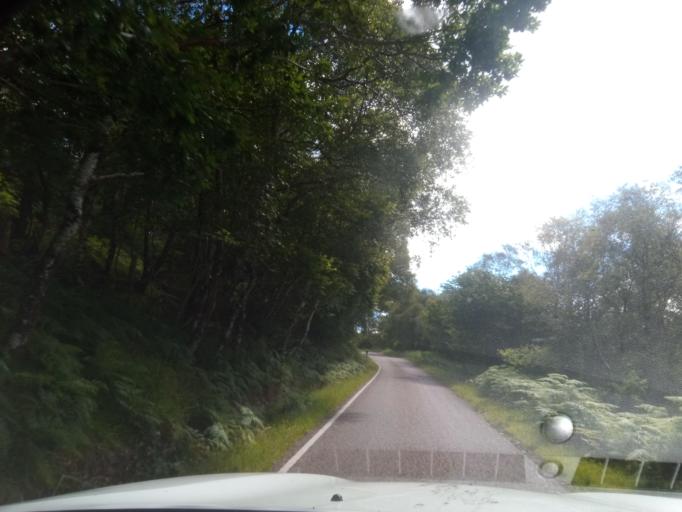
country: GB
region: Scotland
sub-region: Argyll and Bute
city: Isle Of Mull
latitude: 56.7666
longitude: -5.7314
